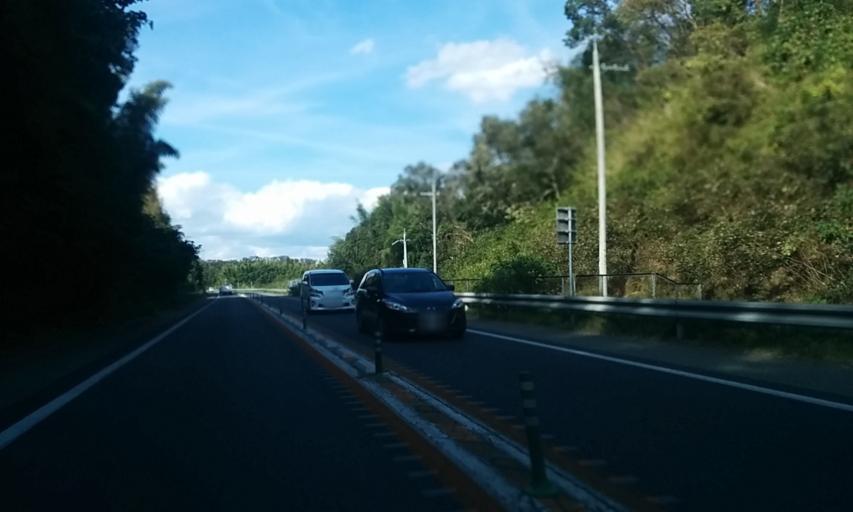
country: JP
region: Kyoto
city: Tanabe
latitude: 34.7610
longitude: 135.7779
